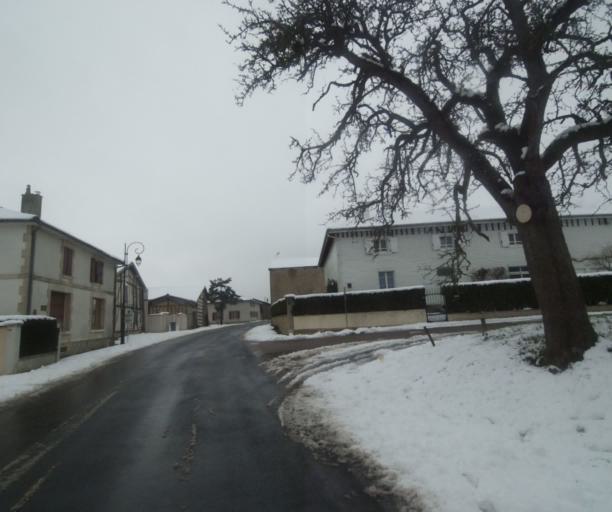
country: FR
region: Champagne-Ardenne
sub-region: Departement de la Haute-Marne
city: Montier-en-Der
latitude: 48.5185
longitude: 4.8224
